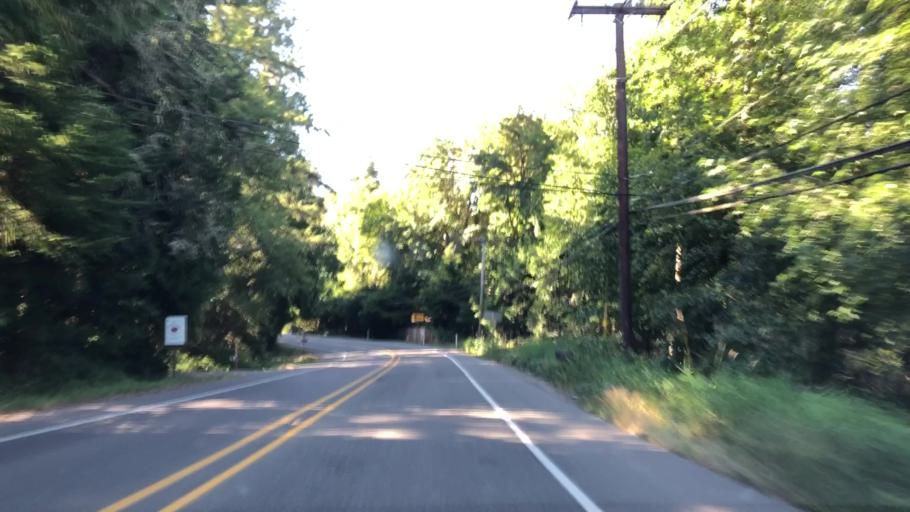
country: US
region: Washington
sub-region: Kitsap County
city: Kingston
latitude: 47.7927
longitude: -122.5058
